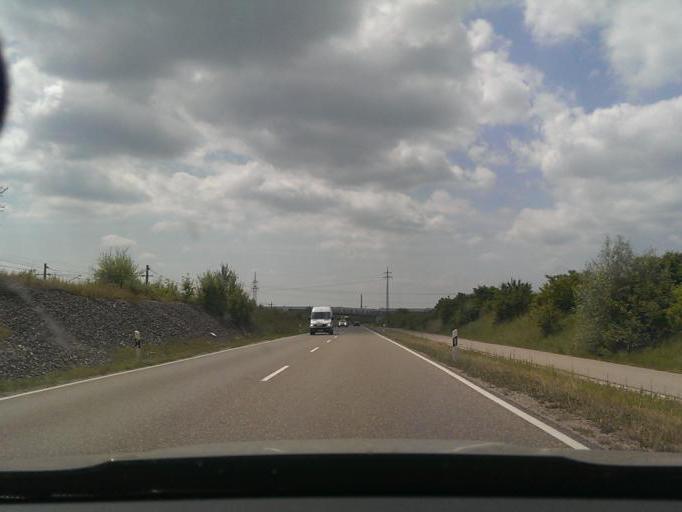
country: DE
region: Bavaria
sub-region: Upper Bavaria
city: Wettstetten
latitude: 48.8037
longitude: 11.4263
